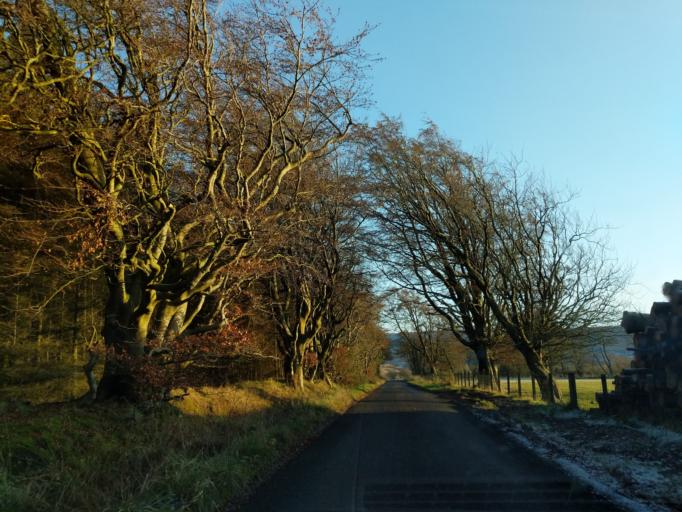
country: GB
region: Scotland
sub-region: Edinburgh
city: Balerno
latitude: 55.8562
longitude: -3.3618
